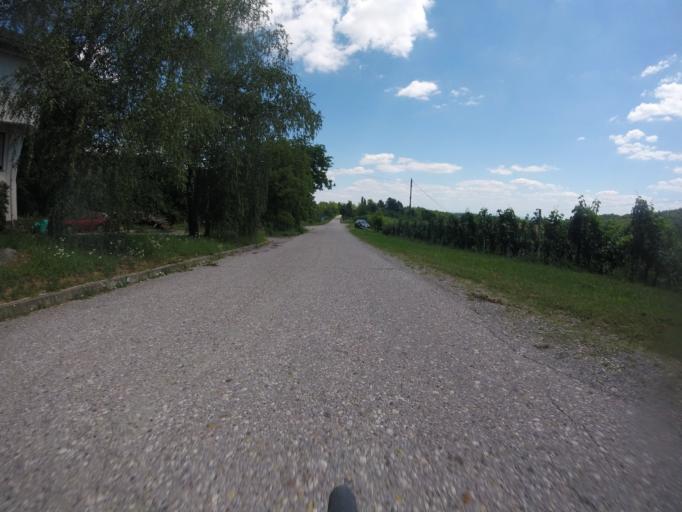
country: HR
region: Karlovacka
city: Ozalj
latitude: 45.6782
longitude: 15.4509
